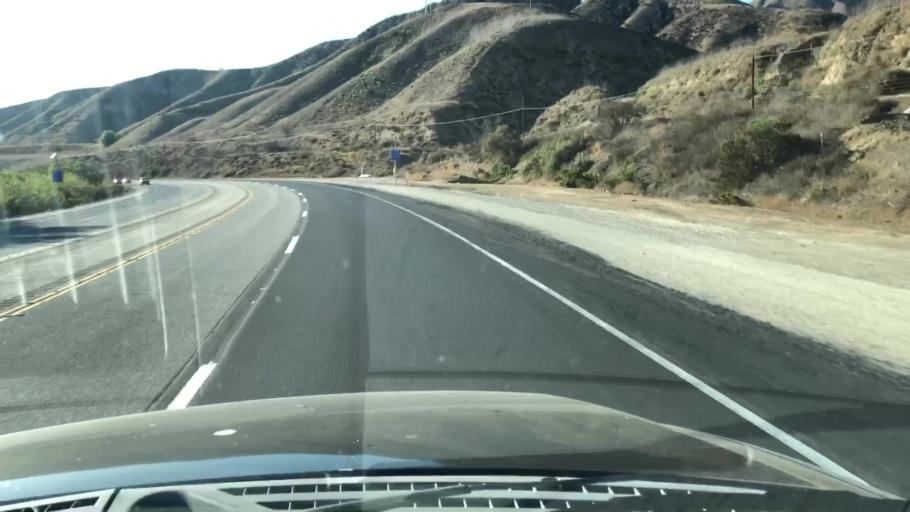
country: US
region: California
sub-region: Ventura County
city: Piru
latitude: 34.4099
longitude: -118.7257
